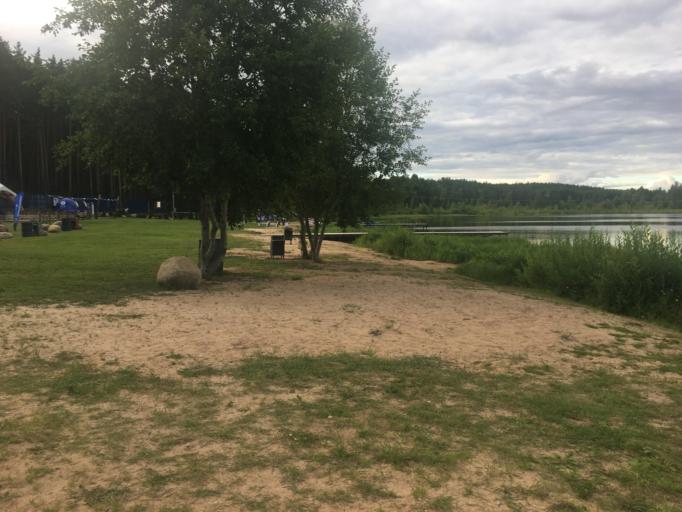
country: RU
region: Pskov
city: Izborsk
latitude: 57.8289
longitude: 27.9545
